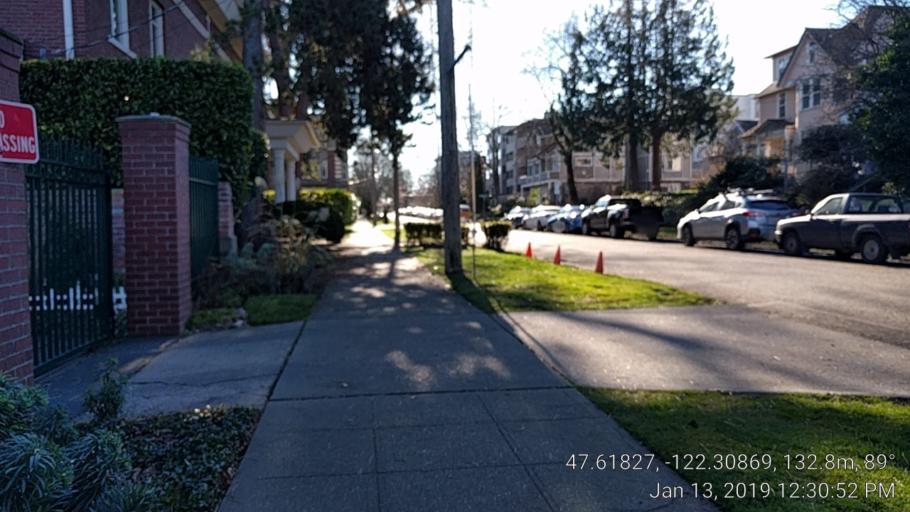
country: US
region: Washington
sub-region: King County
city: Seattle
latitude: 47.6183
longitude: -122.3087
